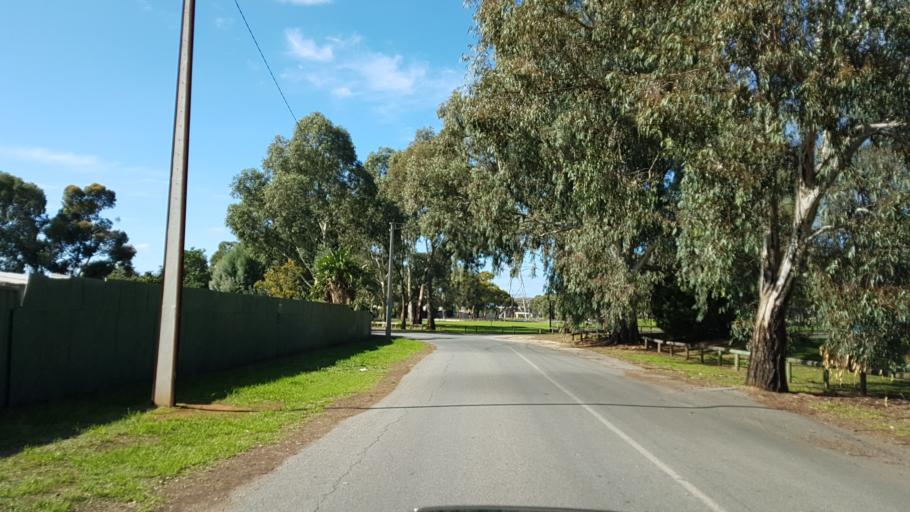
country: AU
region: South Australia
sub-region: Salisbury
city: Salisbury
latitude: -34.7575
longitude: 138.6358
